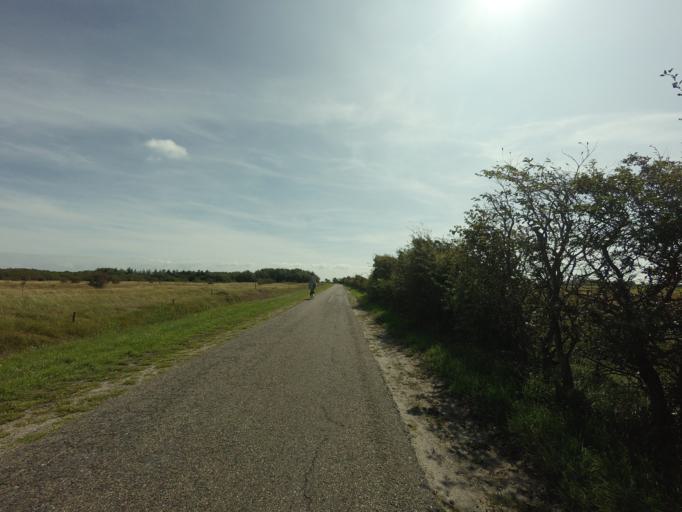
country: NL
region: Friesland
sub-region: Gemeente Ameland
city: Hollum
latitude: 53.4451
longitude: 5.6620
